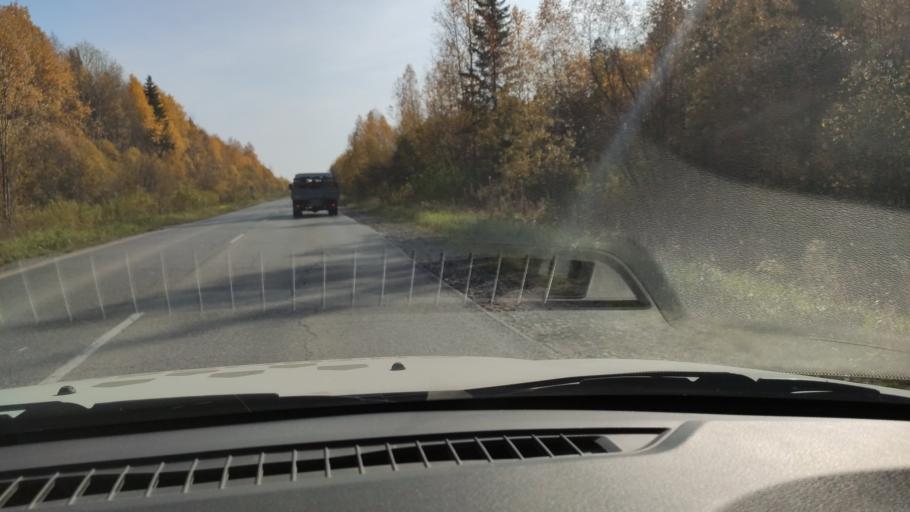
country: RU
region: Perm
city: Novyye Lyady
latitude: 58.0305
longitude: 56.6187
